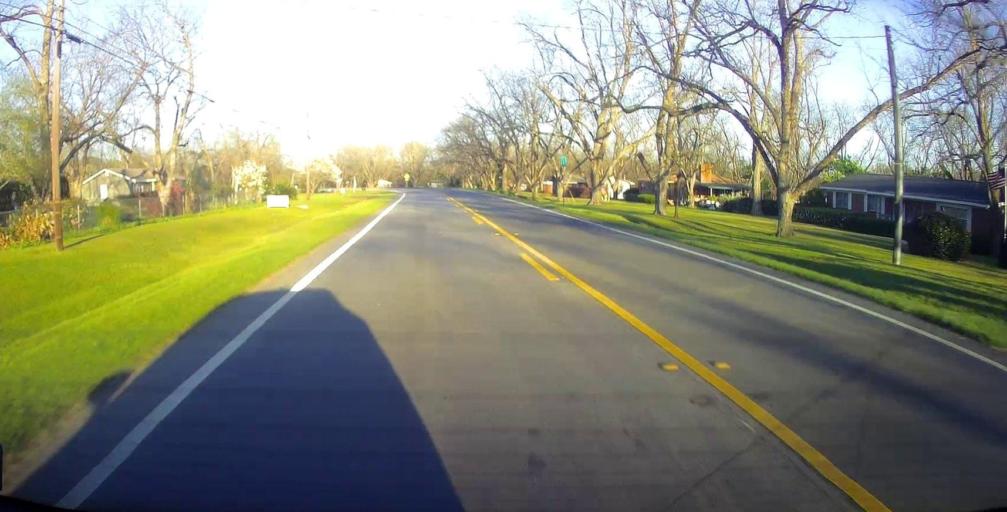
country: US
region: Georgia
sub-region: Wilcox County
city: Rochelle
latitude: 31.9509
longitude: -83.4433
